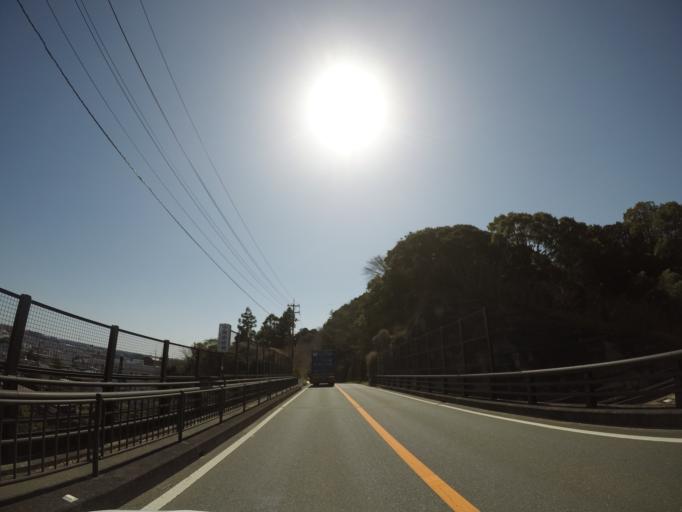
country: JP
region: Shizuoka
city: Kakegawa
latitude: 34.7603
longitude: 138.0810
